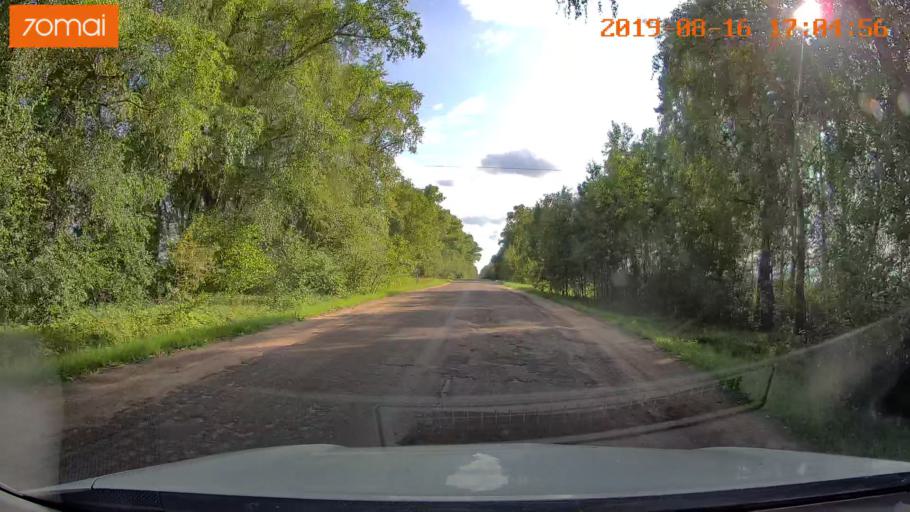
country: BY
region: Mogilev
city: Yalizava
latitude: 53.2411
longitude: 28.9479
